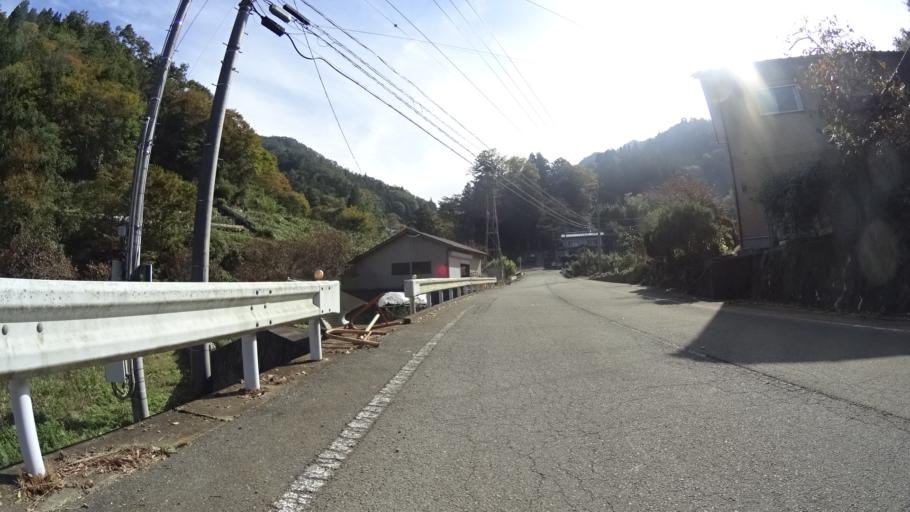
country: JP
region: Yamanashi
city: Otsuki
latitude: 35.5855
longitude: 138.9662
